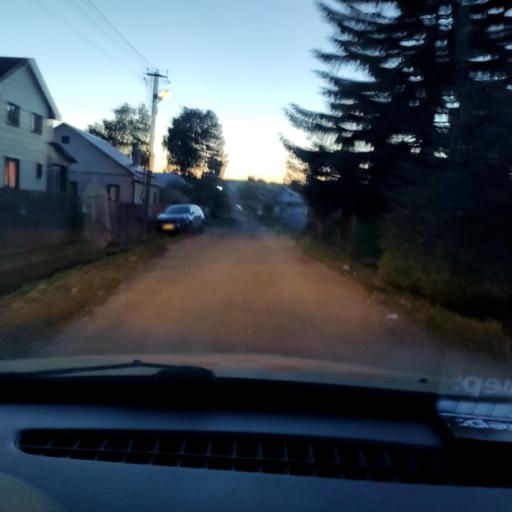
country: RU
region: Bashkortostan
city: Iglino
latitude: 54.8350
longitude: 56.4115
